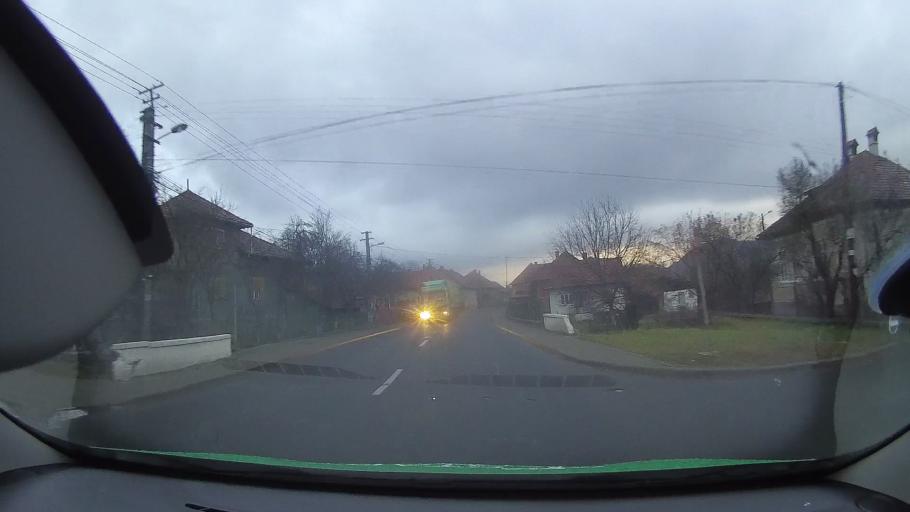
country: RO
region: Hunedoara
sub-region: Municipiul Brad
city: Brad
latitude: 46.1318
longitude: 22.7838
